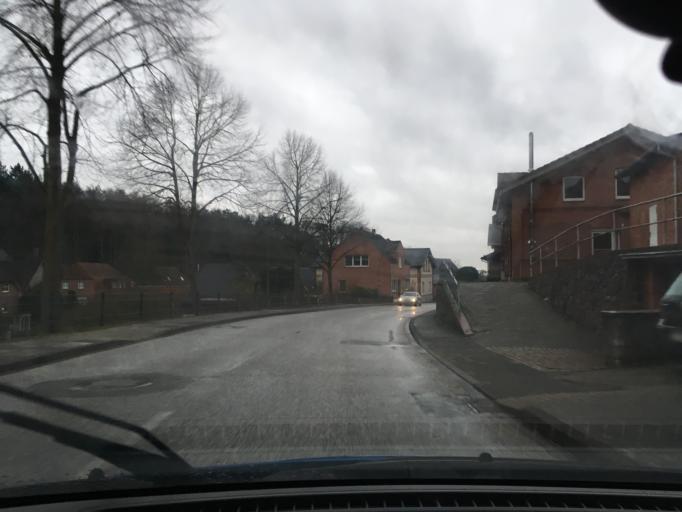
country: DE
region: Lower Saxony
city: Tespe
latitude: 53.4052
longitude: 10.4315
